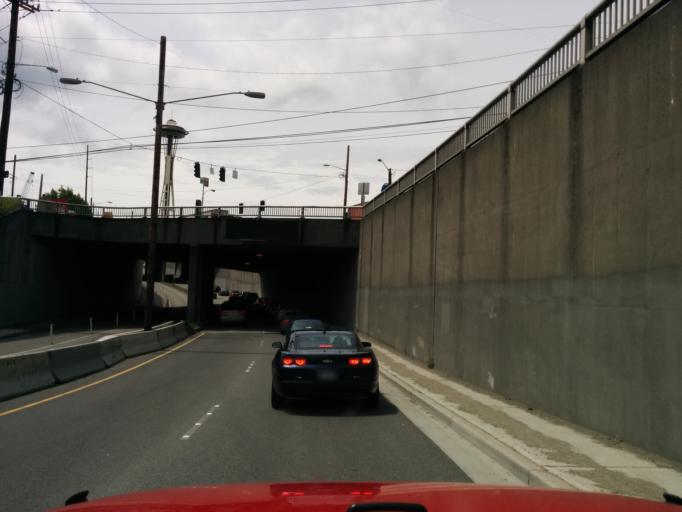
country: US
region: Washington
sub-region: King County
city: Seattle
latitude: 47.6250
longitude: -122.3418
